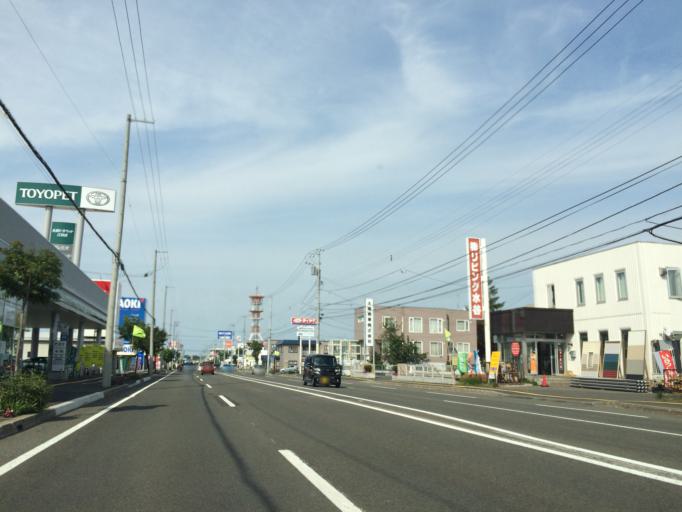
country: JP
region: Hokkaido
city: Ebetsu
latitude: 43.1070
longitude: 141.5432
